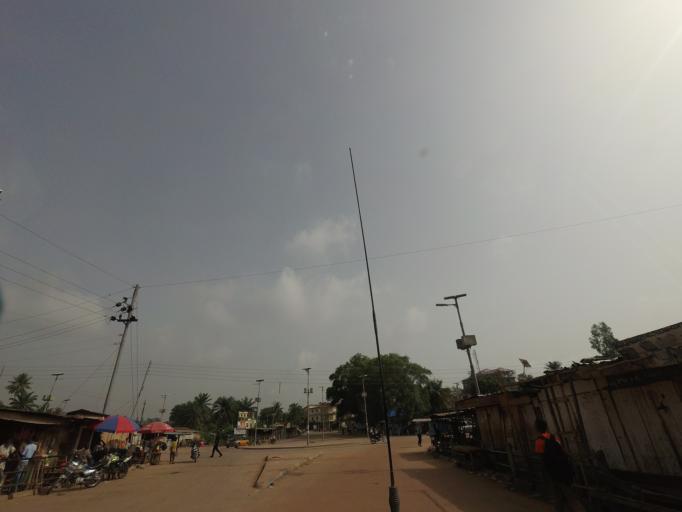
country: SL
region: Southern Province
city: Bo
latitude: 7.9443
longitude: -11.7282
